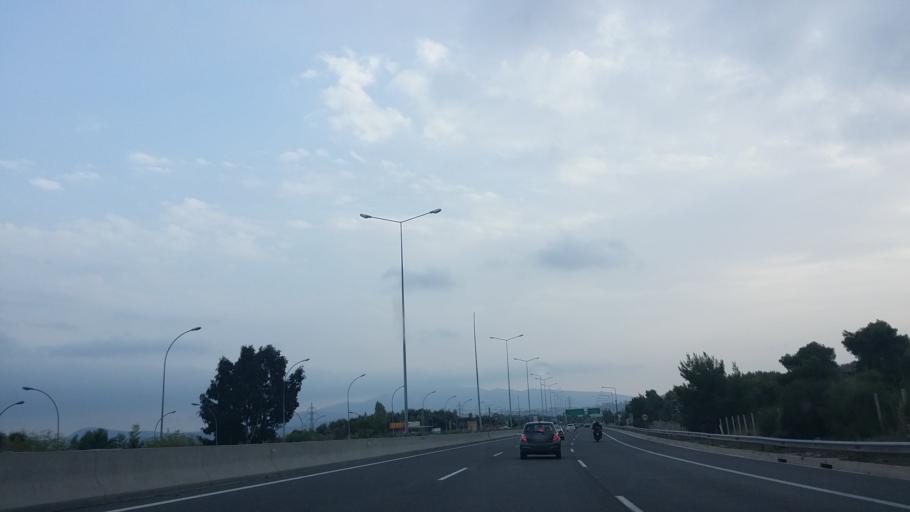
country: GR
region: Attica
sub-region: Nomarchia Anatolikis Attikis
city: Polydendri
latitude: 38.2106
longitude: 23.8552
